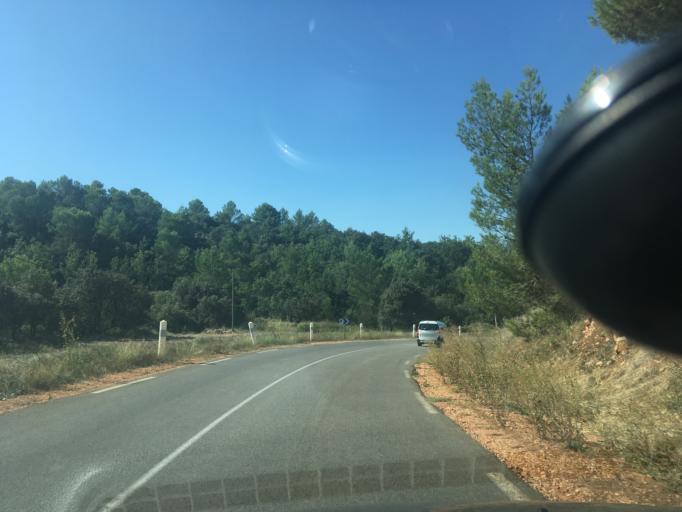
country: FR
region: Provence-Alpes-Cote d'Azur
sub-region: Departement du Var
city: Barjols
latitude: 43.5969
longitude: 6.0381
